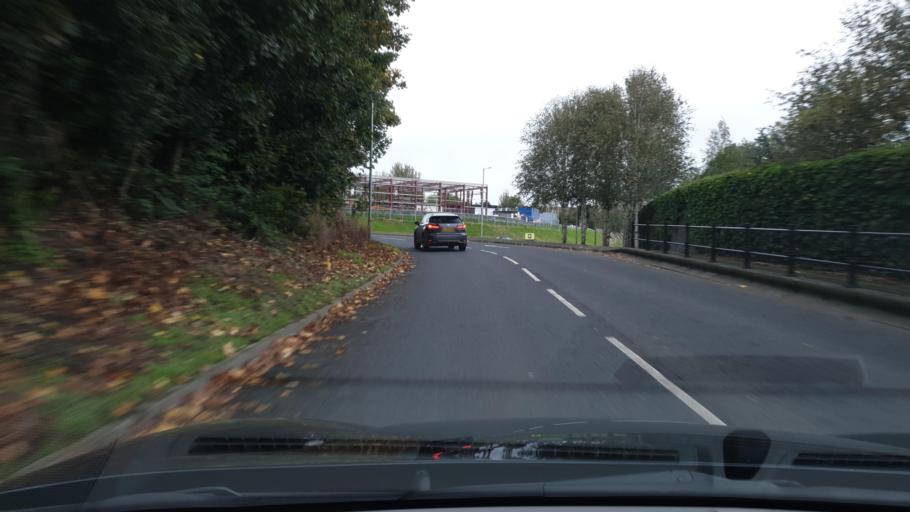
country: GB
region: Northern Ireland
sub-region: Banbridge District
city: Banbridge
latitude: 54.3308
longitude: -6.2776
